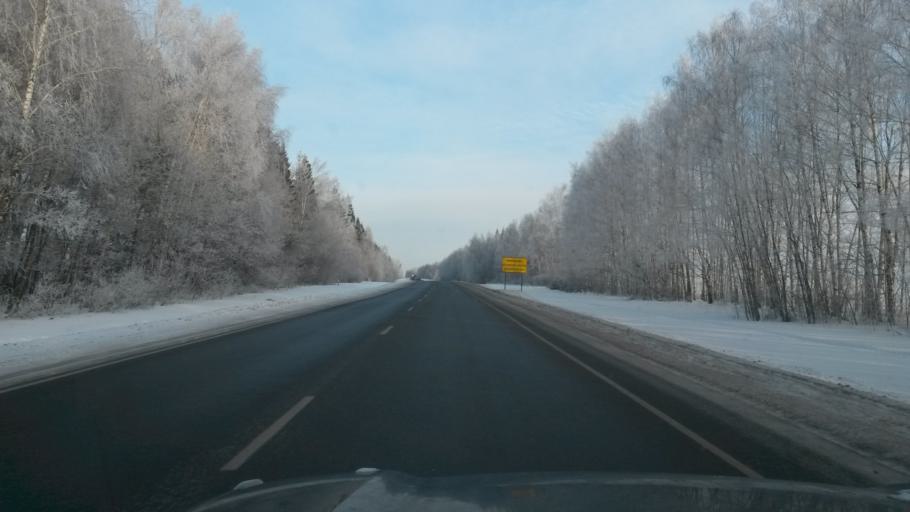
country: RU
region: Vladimir
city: Bogolyubovo
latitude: 56.2274
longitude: 40.4441
